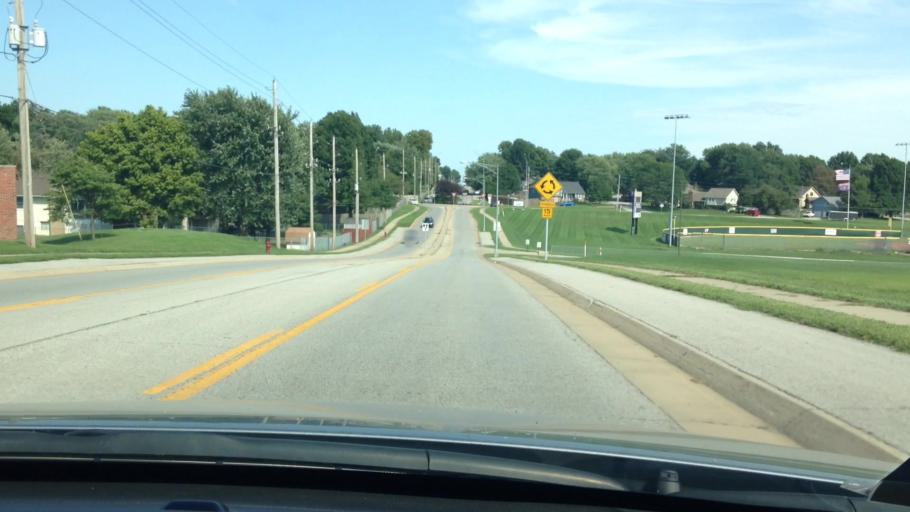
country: US
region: Missouri
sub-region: Cass County
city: Belton
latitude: 38.8157
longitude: -94.5518
